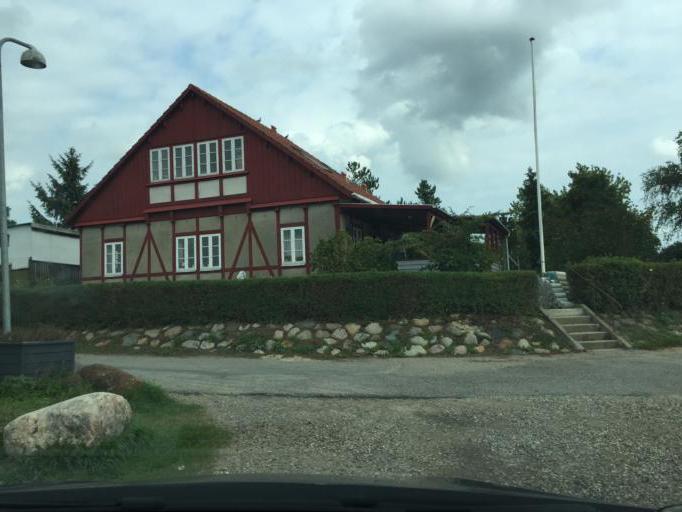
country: DK
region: South Denmark
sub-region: Odense Kommune
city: Stige
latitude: 55.4348
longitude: 10.4172
